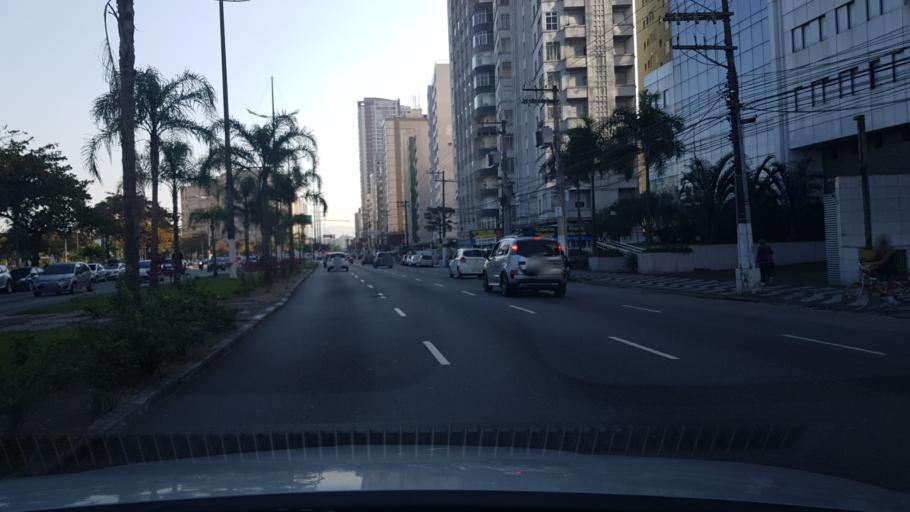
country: BR
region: Sao Paulo
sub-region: Santos
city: Santos
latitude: -23.9678
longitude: -46.3477
